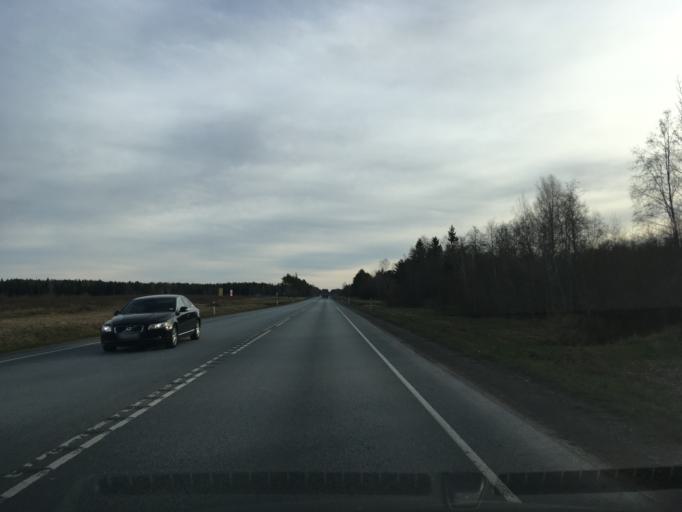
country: EE
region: Ida-Virumaa
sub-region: Johvi vald
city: Johvi
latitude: 59.3678
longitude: 27.4221
